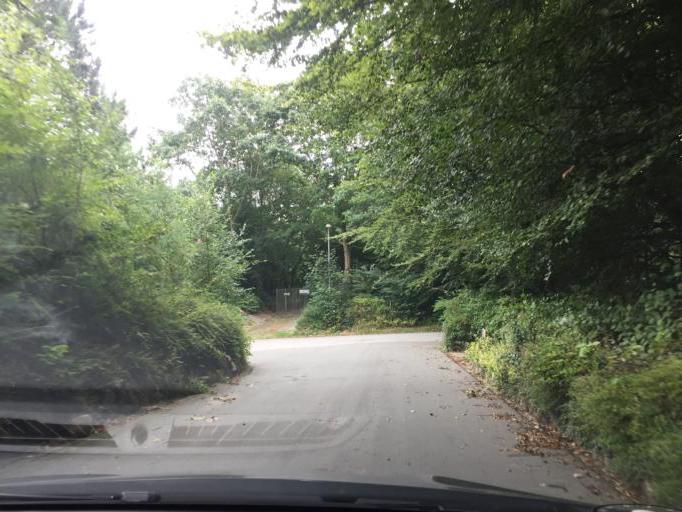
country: DK
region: South Denmark
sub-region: Assens Kommune
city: Arup
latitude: 55.3842
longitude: 10.0466
